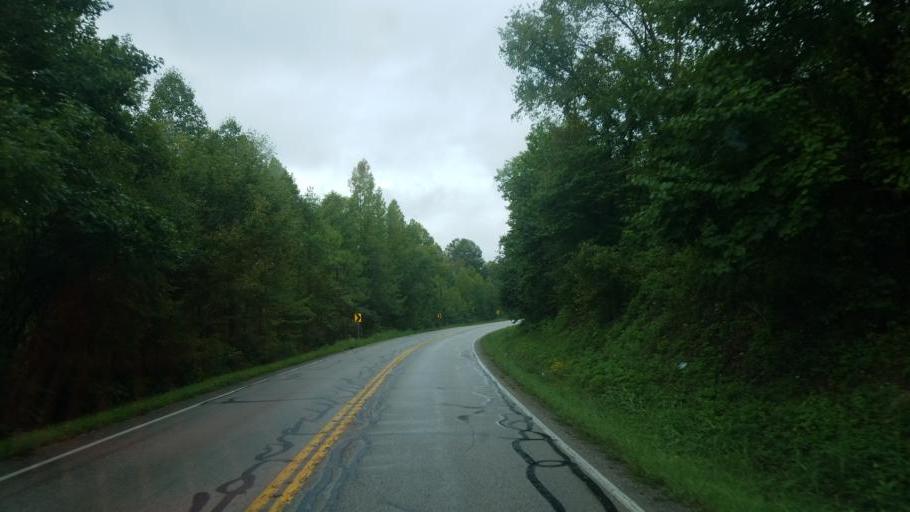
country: US
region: Kentucky
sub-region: Rowan County
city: Morehead
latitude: 38.1499
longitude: -83.4800
